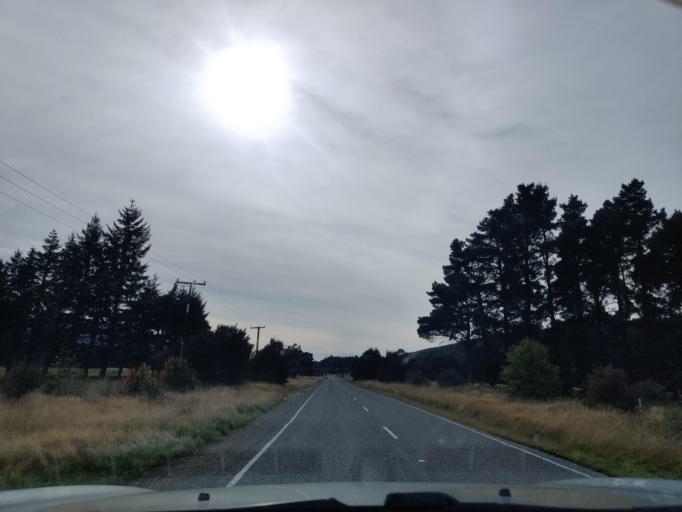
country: NZ
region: Tasman
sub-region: Tasman District
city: Brightwater
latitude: -41.6663
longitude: 173.1993
